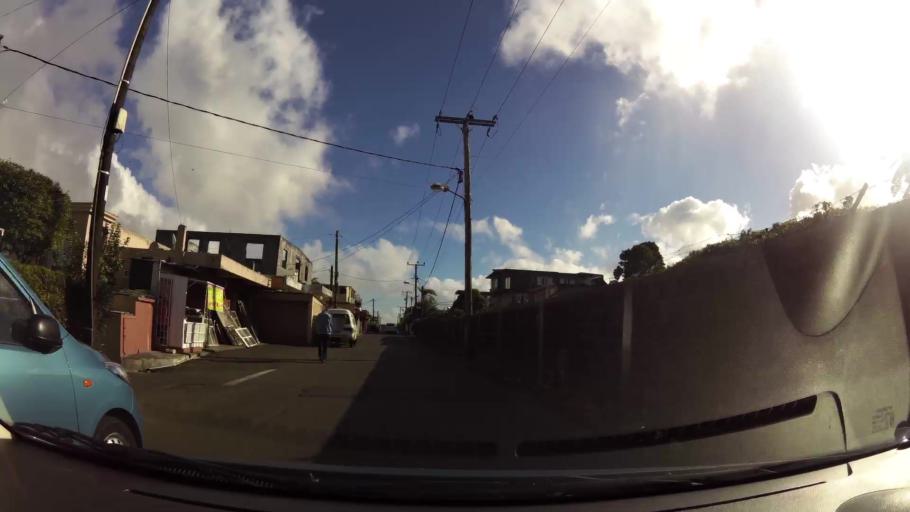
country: MU
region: Plaines Wilhems
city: Curepipe
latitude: -20.3235
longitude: 57.5097
